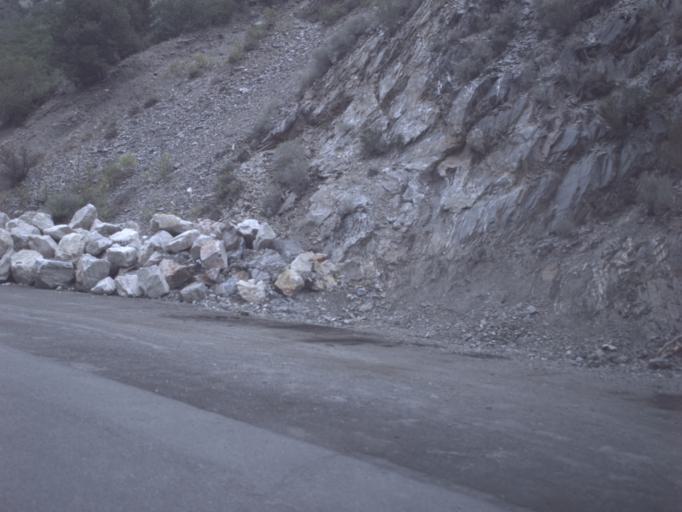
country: US
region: Utah
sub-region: Utah County
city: Cedar Hills
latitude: 40.4337
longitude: -111.7429
